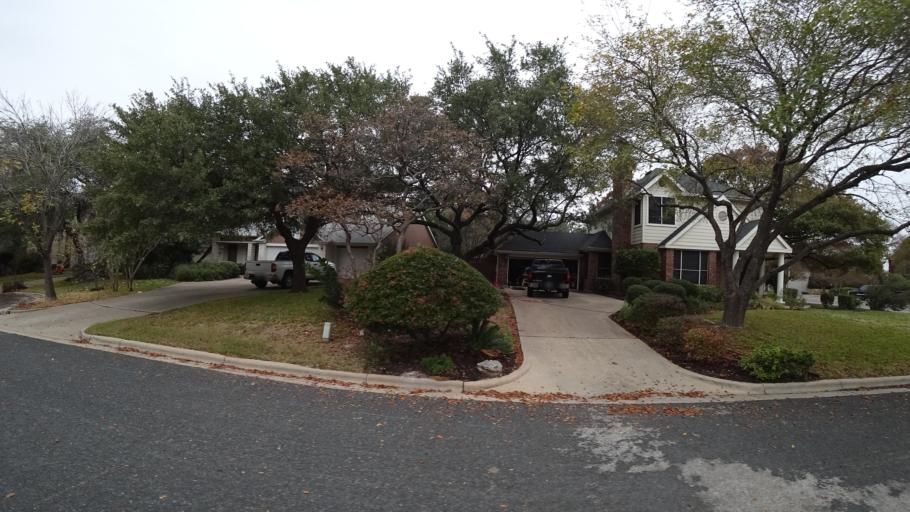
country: US
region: Texas
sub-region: Williamson County
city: Jollyville
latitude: 30.3828
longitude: -97.7993
